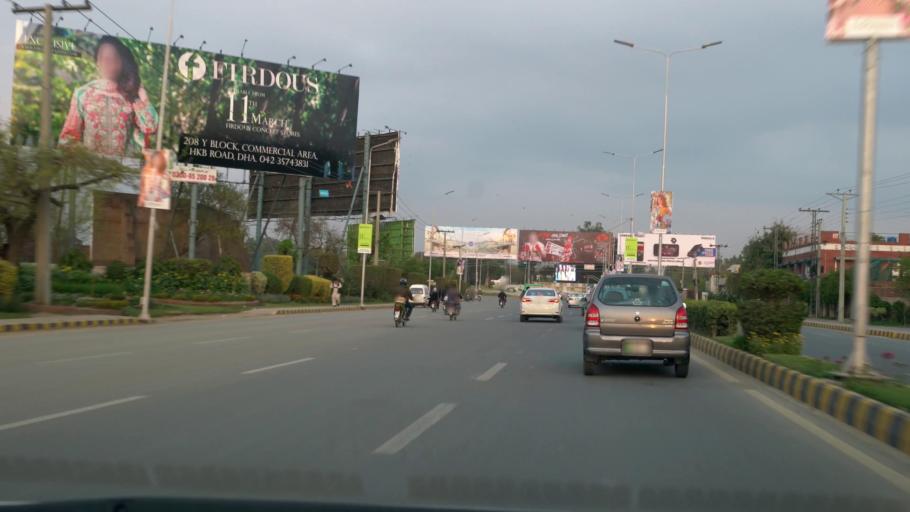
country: PK
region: Punjab
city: Lahore
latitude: 31.5016
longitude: 74.3669
